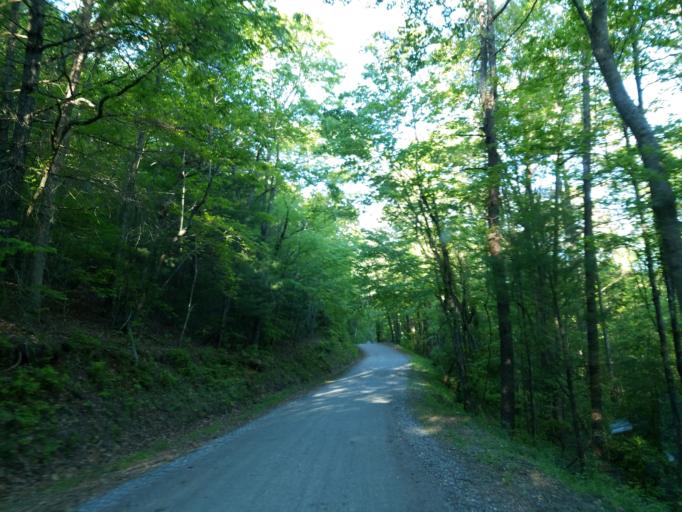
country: US
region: Georgia
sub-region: Fannin County
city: Blue Ridge
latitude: 34.7514
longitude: -84.2742
